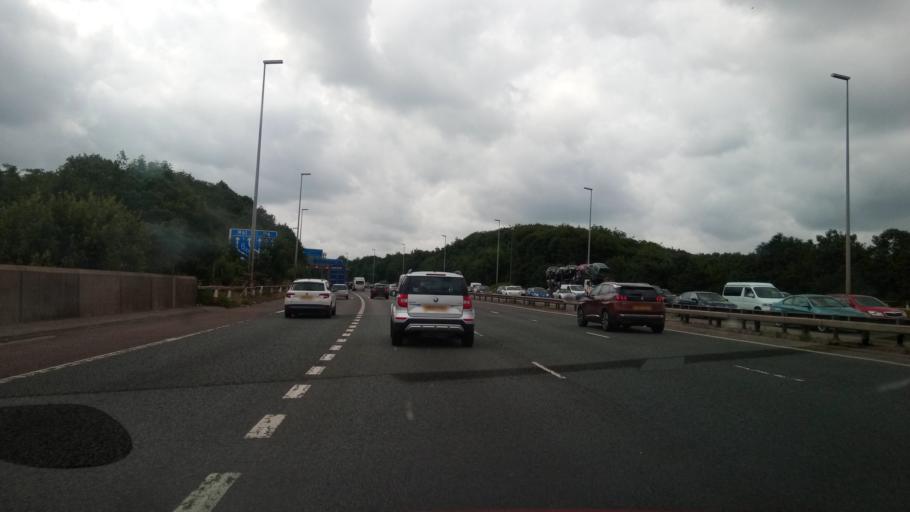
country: GB
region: England
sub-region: Lancashire
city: Clayton-le-Woods
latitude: 53.7439
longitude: -2.6502
